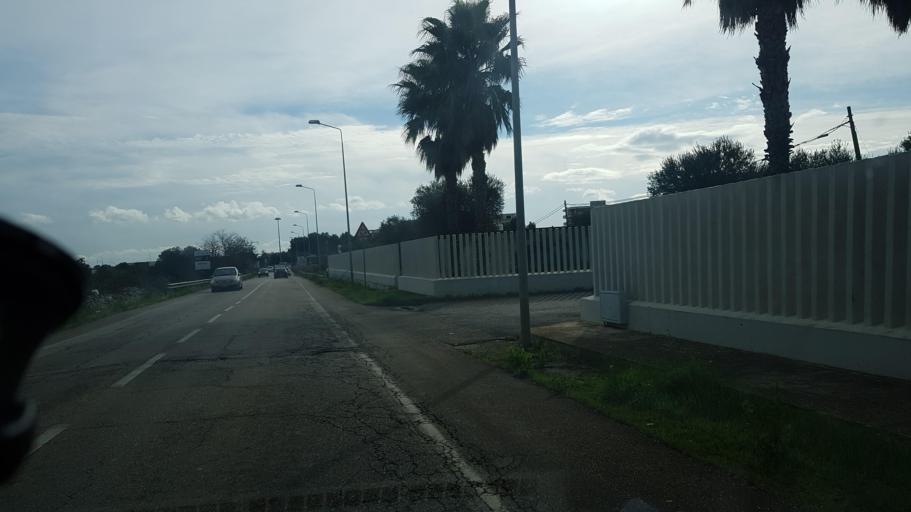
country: IT
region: Apulia
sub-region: Provincia di Brindisi
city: San Vito dei Normanni
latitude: 40.6677
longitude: 17.6969
